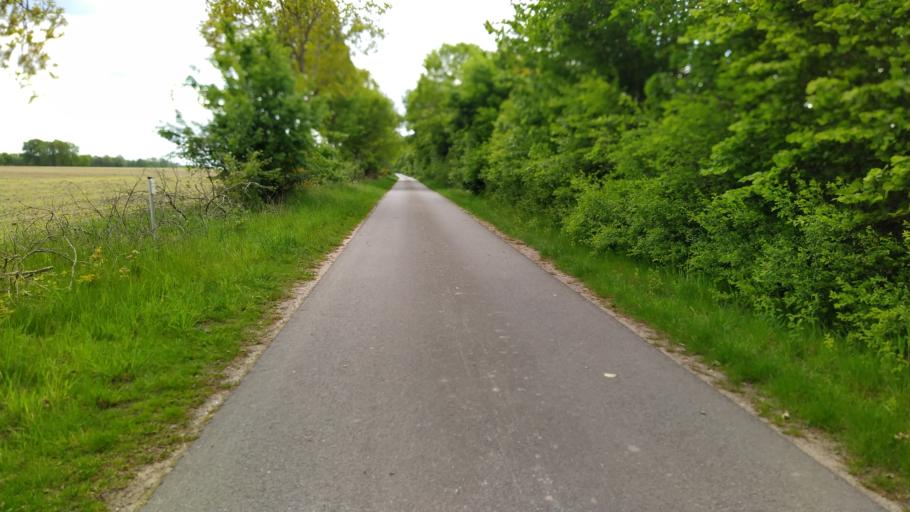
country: DE
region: Lower Saxony
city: Ahlerstedt
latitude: 53.3747
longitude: 9.3968
